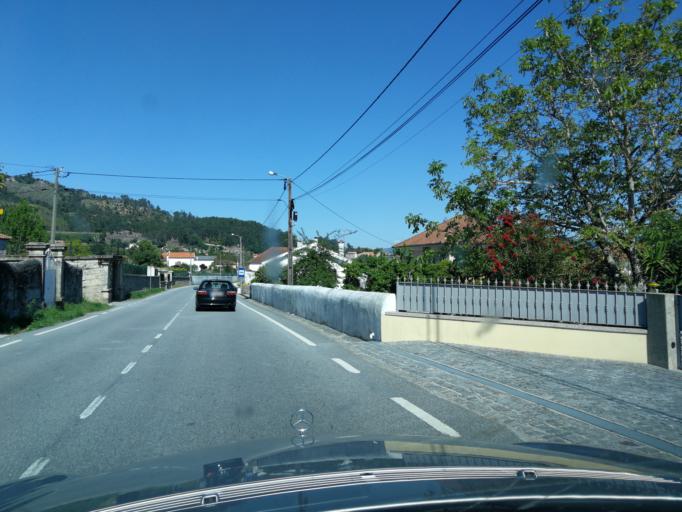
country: PT
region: Viana do Castelo
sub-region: Viana do Castelo
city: Darque
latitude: 41.7112
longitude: -8.7607
